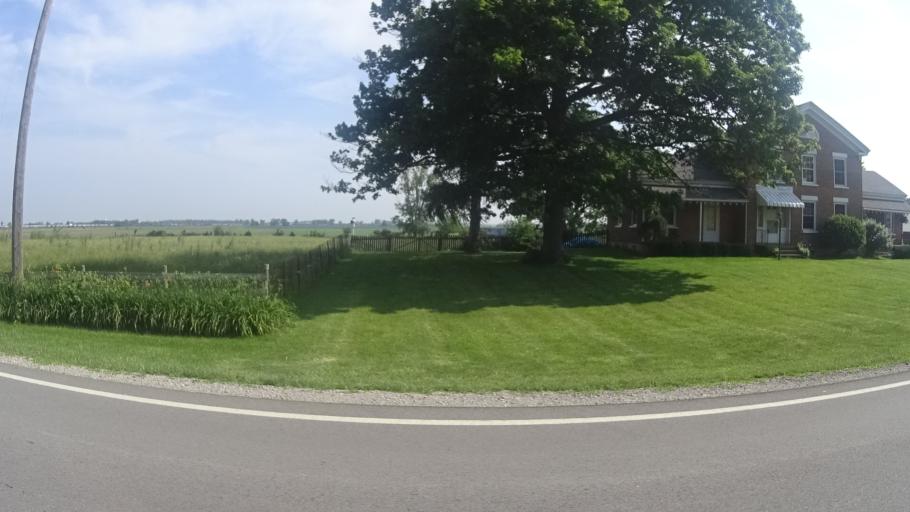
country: US
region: Ohio
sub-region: Huron County
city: Monroeville
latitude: 41.2881
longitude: -82.7419
